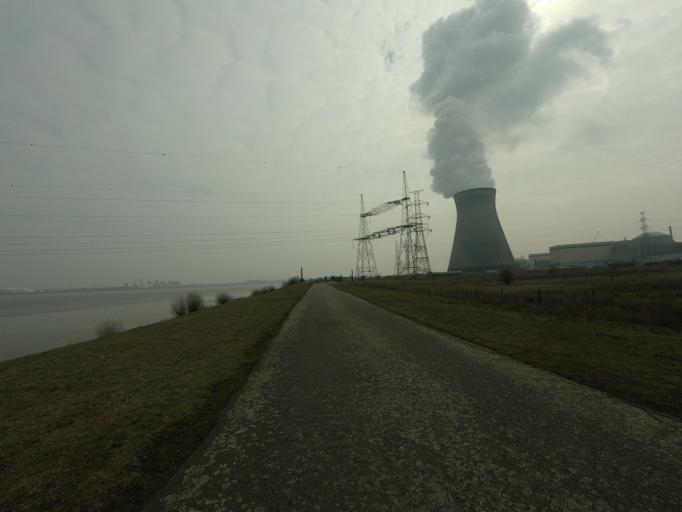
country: NL
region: North Brabant
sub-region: Gemeente Woensdrecht
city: Woensdrecht
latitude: 51.3324
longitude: 4.2587
